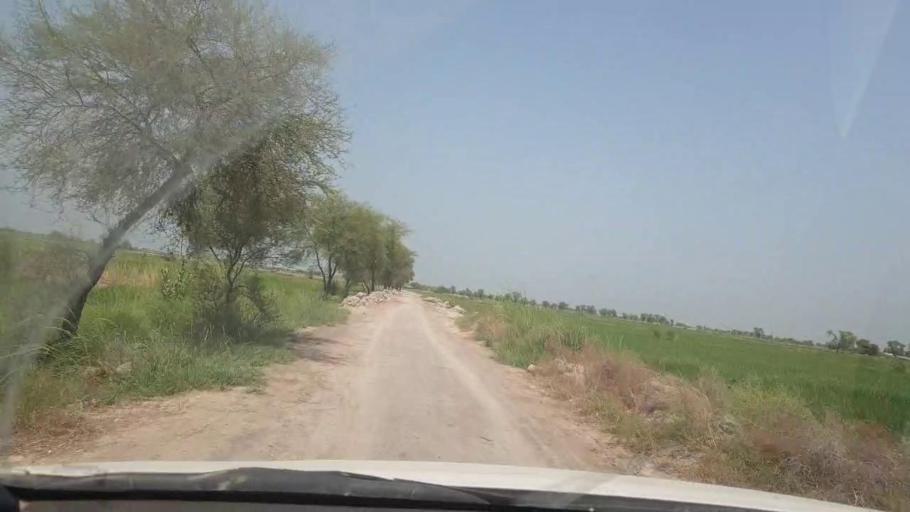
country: PK
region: Sindh
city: Lakhi
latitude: 27.8711
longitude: 68.7323
